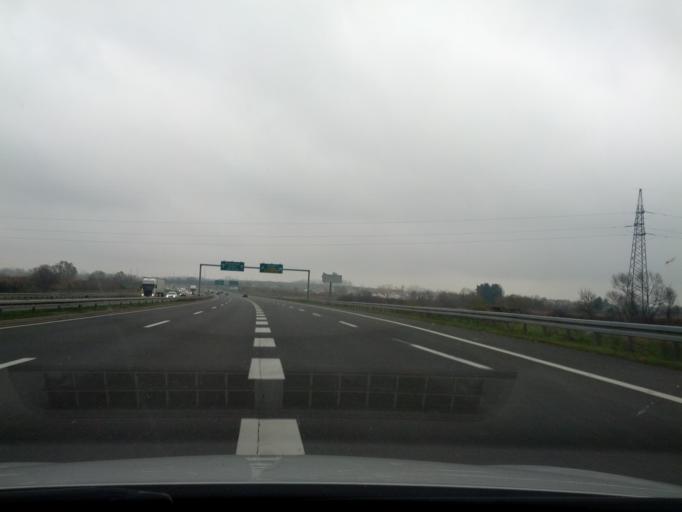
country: HR
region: Zagrebacka
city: Rakitje
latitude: 45.7837
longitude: 15.8213
